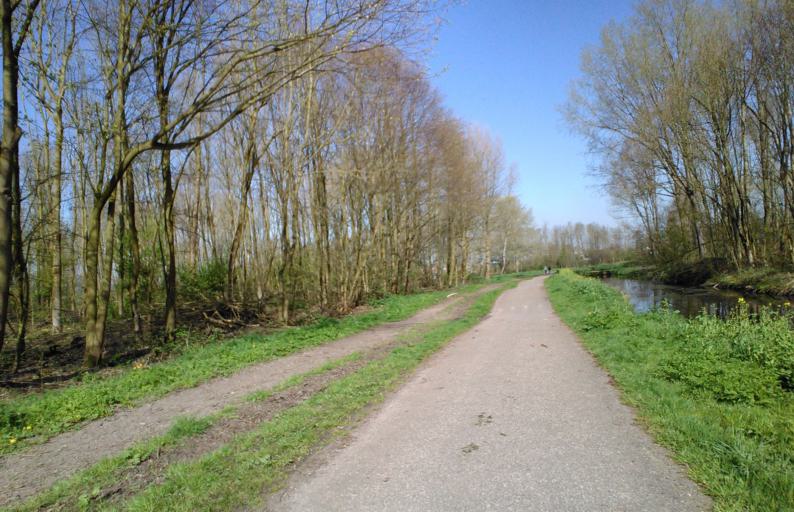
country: NL
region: South Holland
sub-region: Gemeente Krimpen aan den IJssel
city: Krimpen aan den IJssel
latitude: 51.9639
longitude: 4.6301
